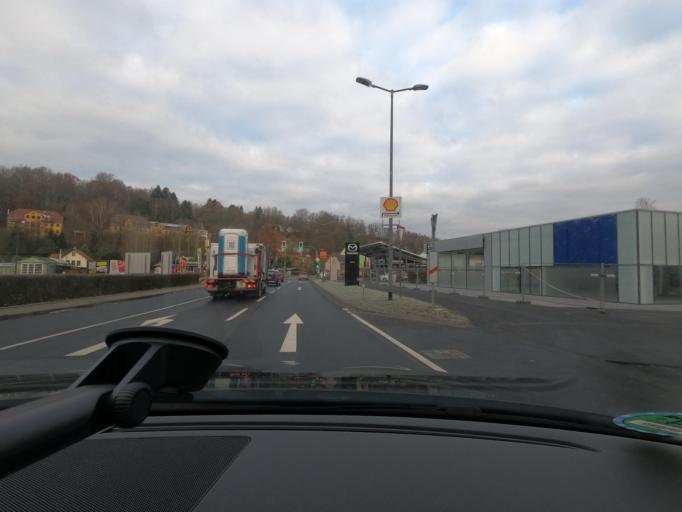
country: DE
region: Thuringia
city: Schleusingen
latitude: 50.5135
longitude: 10.7537
